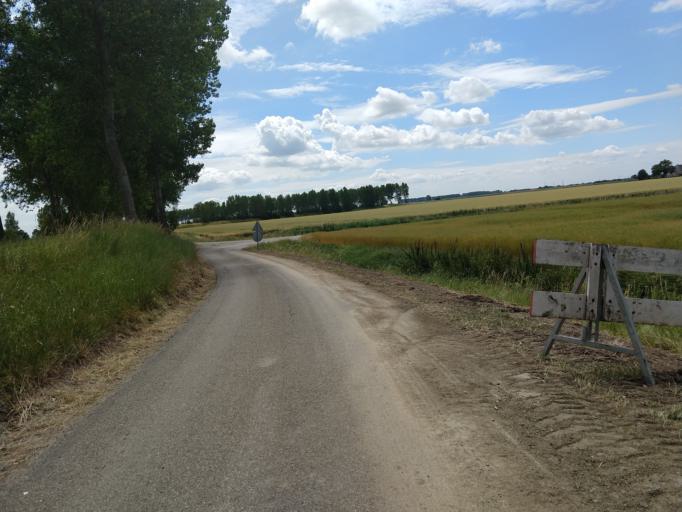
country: NL
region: Zeeland
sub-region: Gemeente Noord-Beveland
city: Kamperland
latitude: 51.5311
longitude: 3.7836
